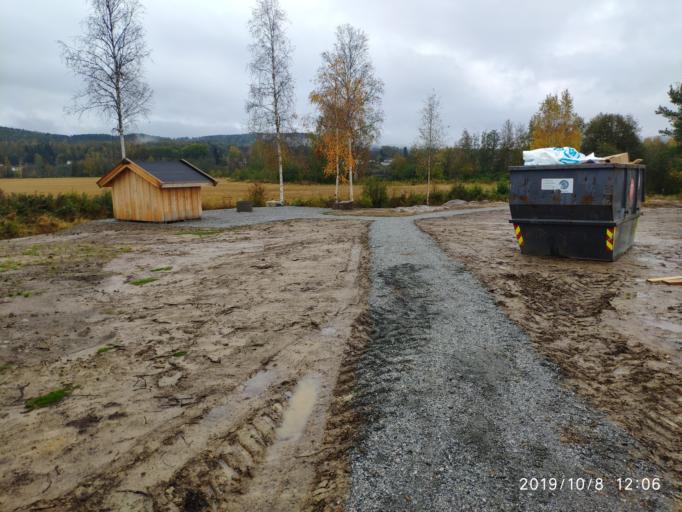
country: NO
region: Akershus
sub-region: Nes
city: Arnes
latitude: 60.1700
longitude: 11.5501
